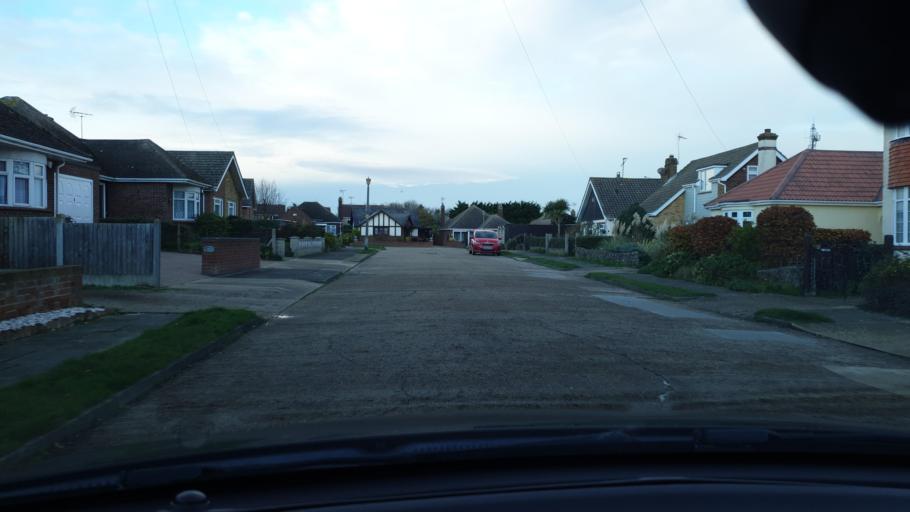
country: GB
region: England
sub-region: Essex
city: Clacton-on-Sea
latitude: 51.8017
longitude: 1.1686
